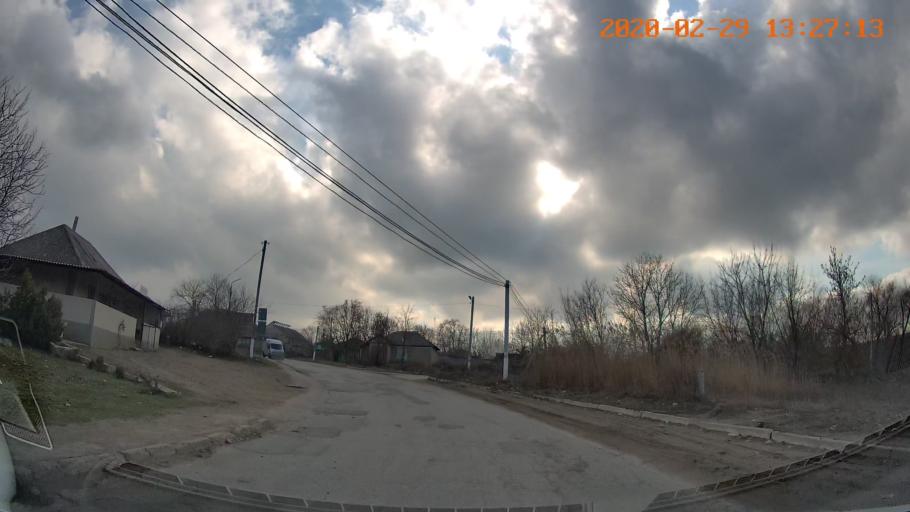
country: MD
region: Telenesti
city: Camenca
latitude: 47.9134
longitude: 28.6396
